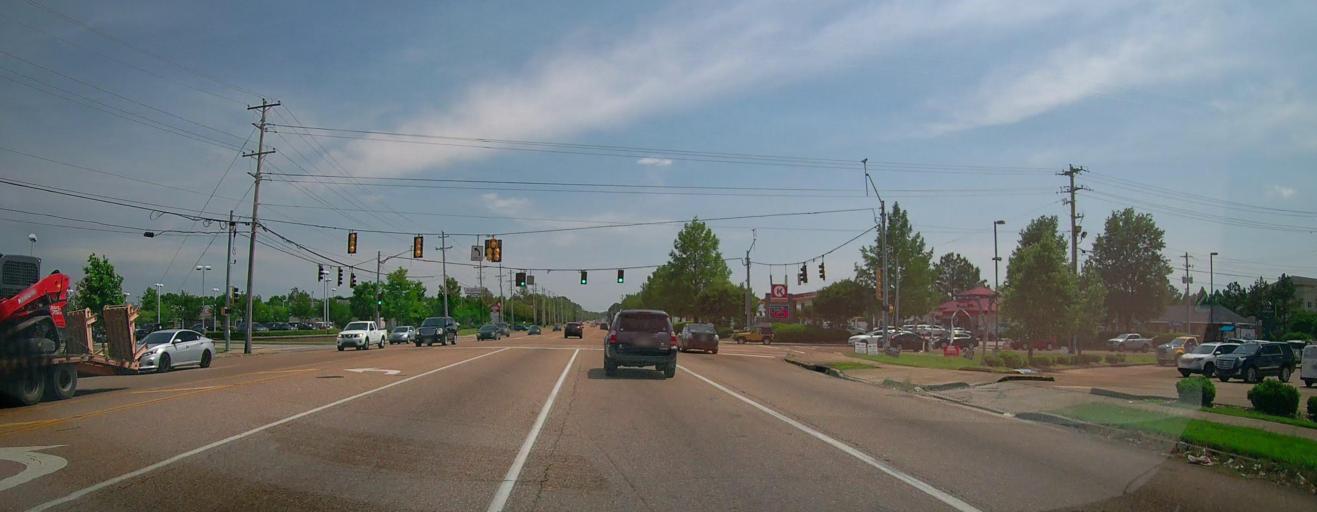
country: US
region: Tennessee
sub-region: Shelby County
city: Germantown
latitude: 35.0357
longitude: -89.7959
